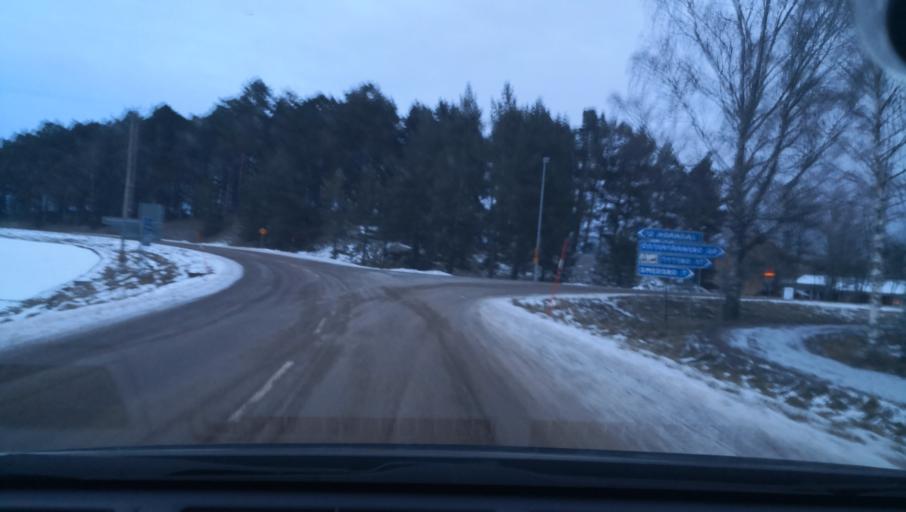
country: SE
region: Dalarna
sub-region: Avesta Kommun
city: Horndal
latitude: 60.2036
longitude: 16.4757
